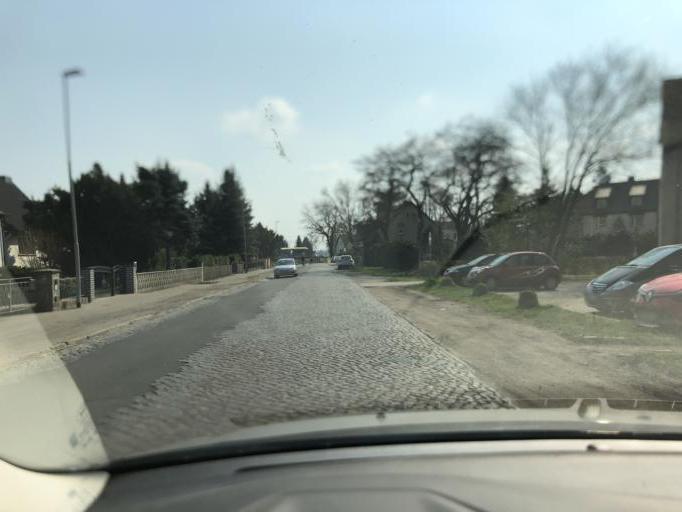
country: DE
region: Saxony-Anhalt
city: Hohenthurm
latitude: 51.5142
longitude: 12.0969
